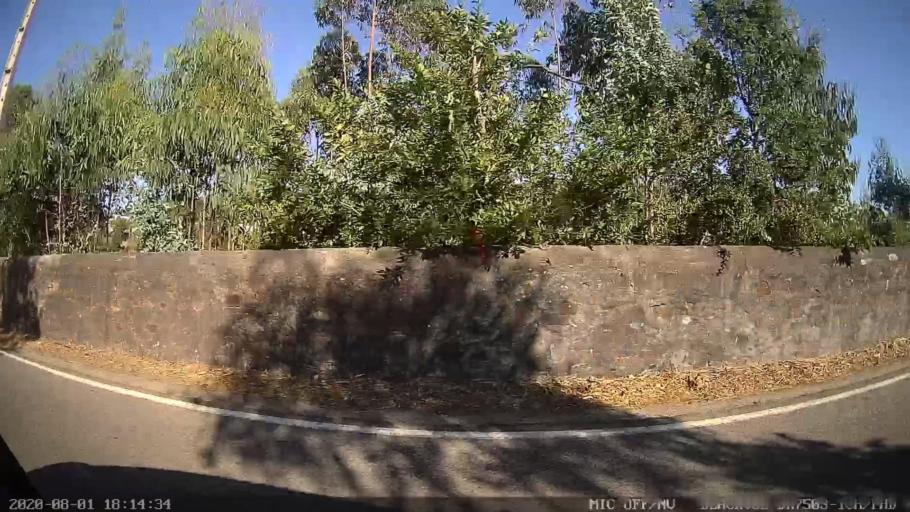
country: PT
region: Porto
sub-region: Pacos de Ferreira
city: Seroa
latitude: 41.2691
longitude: -8.4707
